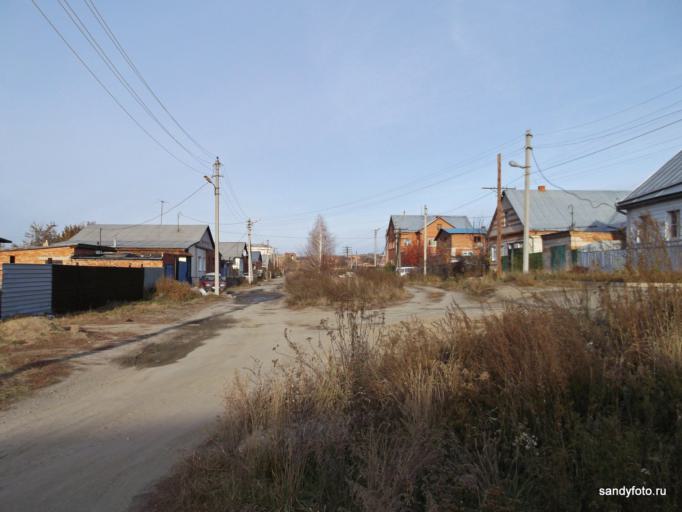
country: RU
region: Chelyabinsk
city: Troitsk
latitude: 54.0729
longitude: 61.5876
